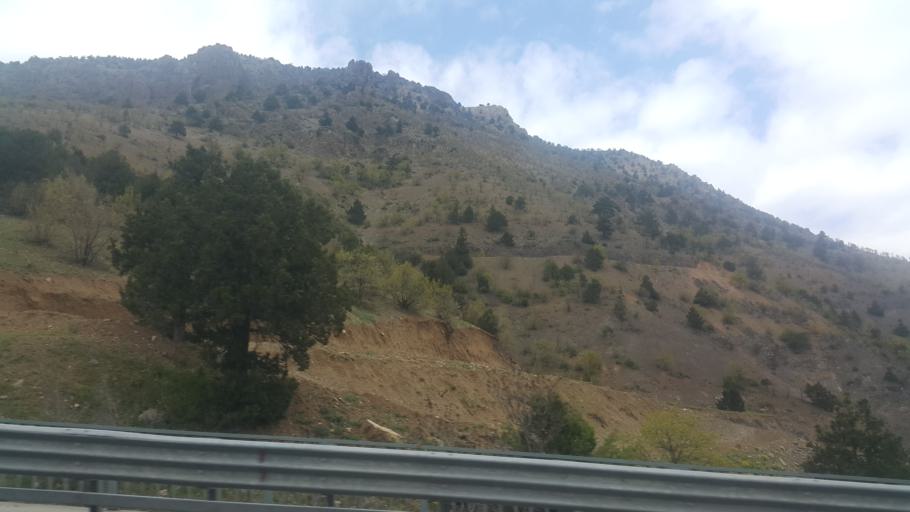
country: TR
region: Nigde
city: Ciftehan
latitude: 37.5322
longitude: 34.8075
